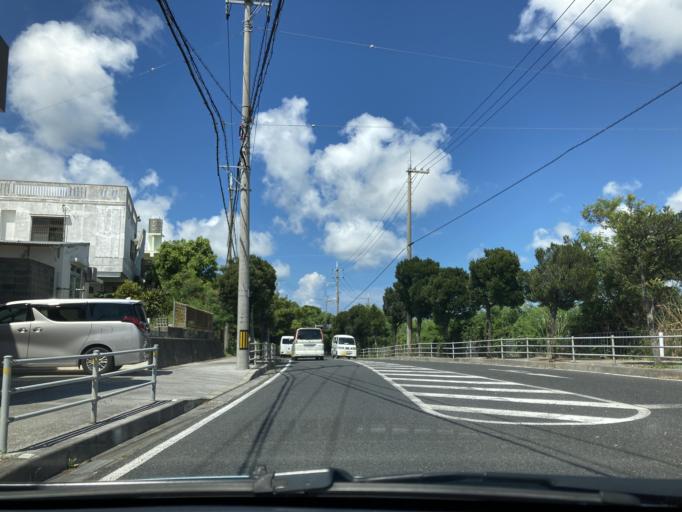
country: JP
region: Okinawa
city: Tomigusuku
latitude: 26.1719
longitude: 127.7220
